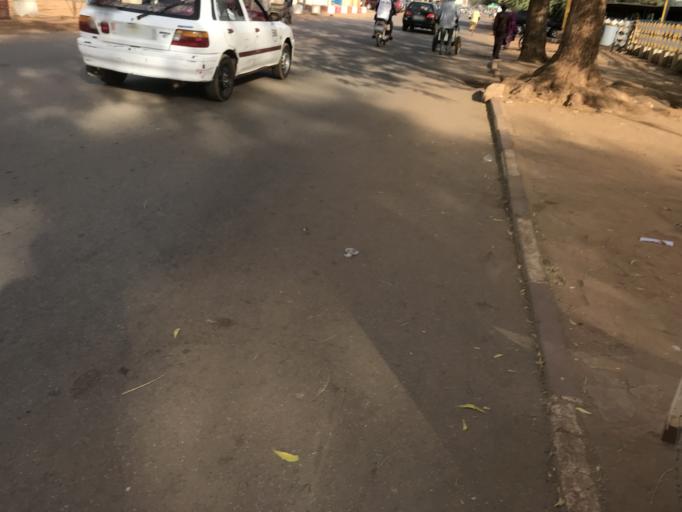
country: NE
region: Niamey
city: Niamey
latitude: 13.5098
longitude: 2.1145
